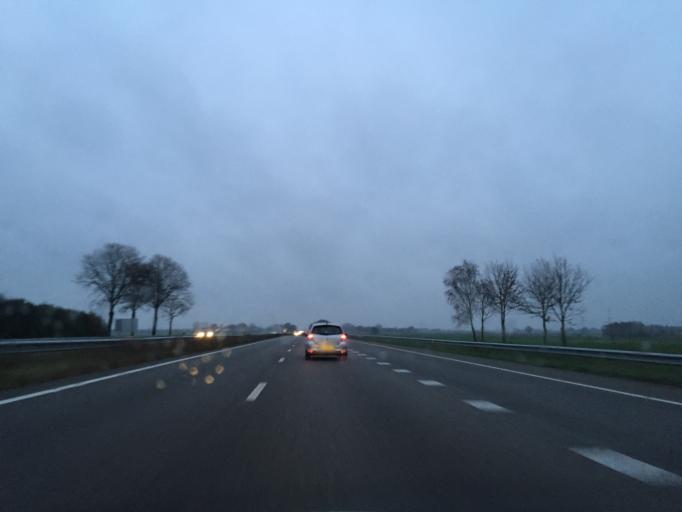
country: NL
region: North Brabant
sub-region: Gemeente Bergen op Zoom
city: Bergen op Zoom
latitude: 51.5072
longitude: 4.3654
